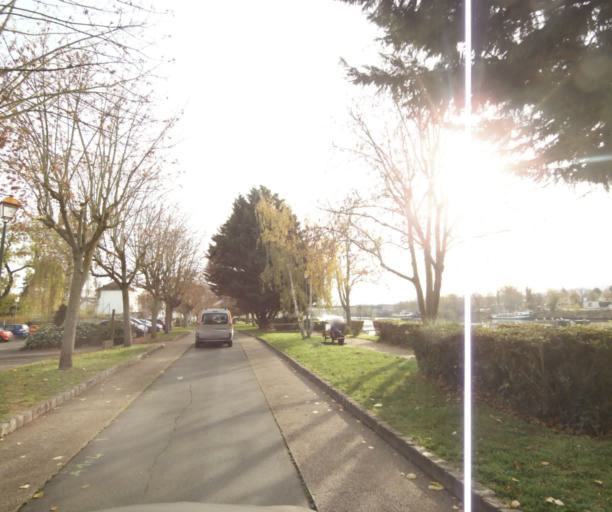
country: FR
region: Ile-de-France
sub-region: Departement des Yvelines
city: Triel-sur-Seine
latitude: 48.9817
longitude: 2.0004
